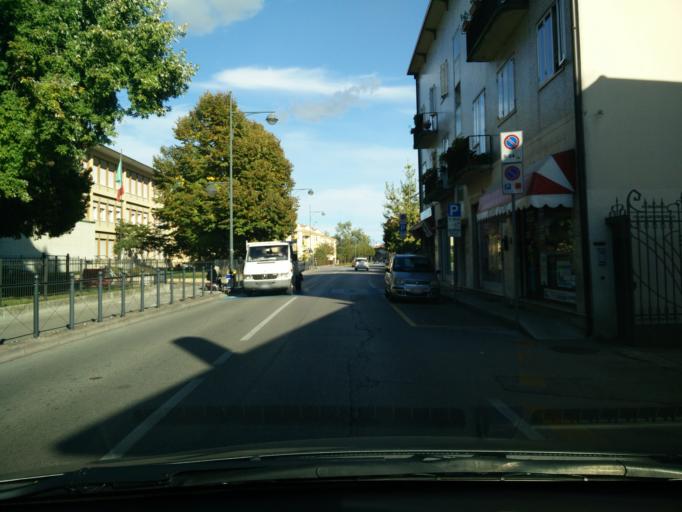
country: IT
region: Veneto
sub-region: Provincia di Venezia
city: San Dona di Piave
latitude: 45.6318
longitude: 12.5688
